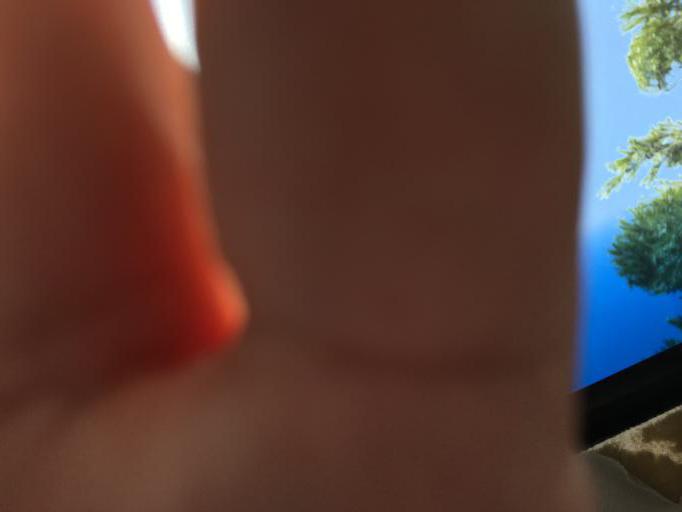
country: US
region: California
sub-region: Los Angeles County
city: Charter Oak
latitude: 34.0695
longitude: -117.8551
